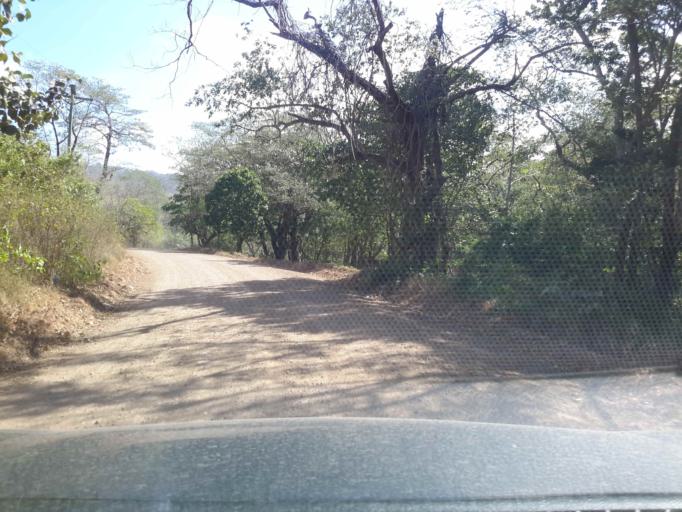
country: NI
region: Rivas
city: San Juan del Sur
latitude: 11.1885
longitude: -85.8062
